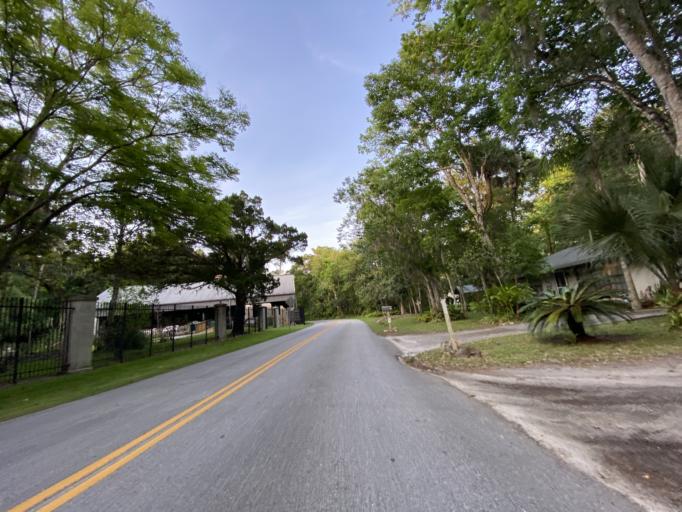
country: US
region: Florida
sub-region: Volusia County
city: Port Orange
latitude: 29.1409
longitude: -81.0060
